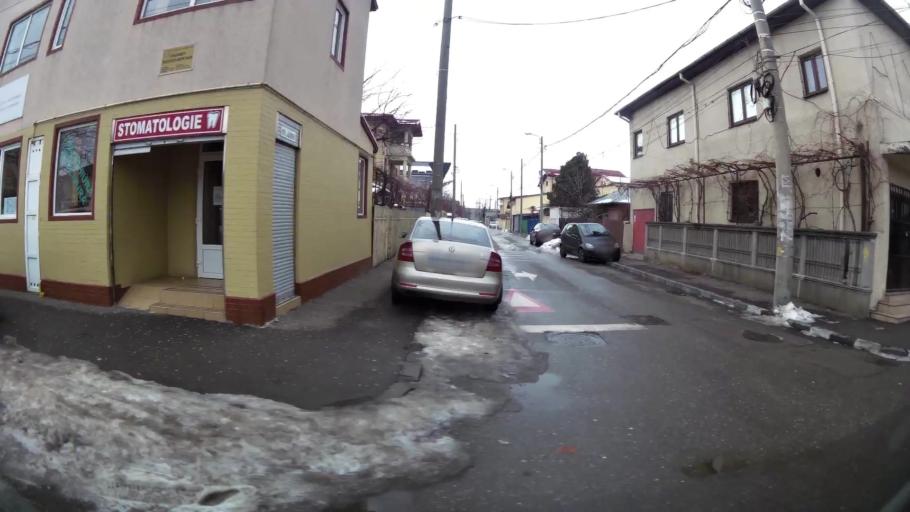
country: RO
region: Ilfov
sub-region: Comuna Pantelimon
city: Pantelimon
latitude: 44.4339
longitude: 26.1984
